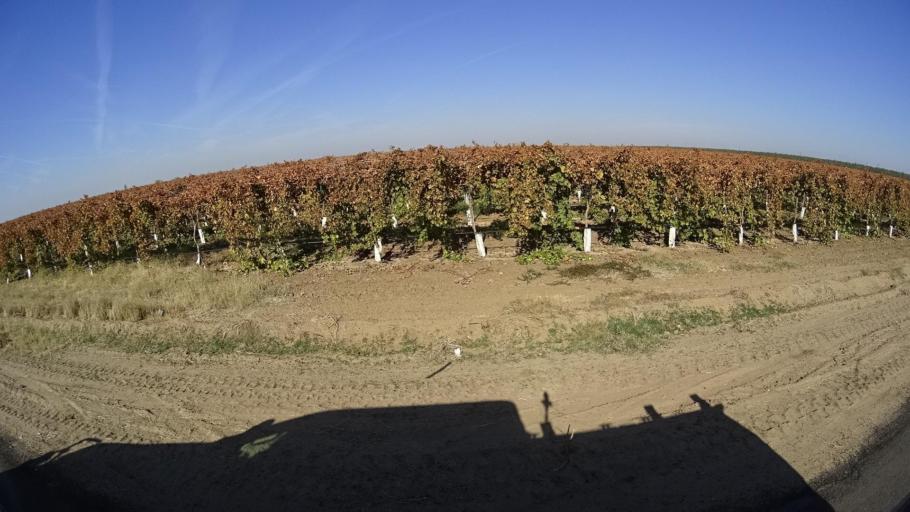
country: US
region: California
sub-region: Kern County
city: McFarland
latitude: 35.6456
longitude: -119.1902
